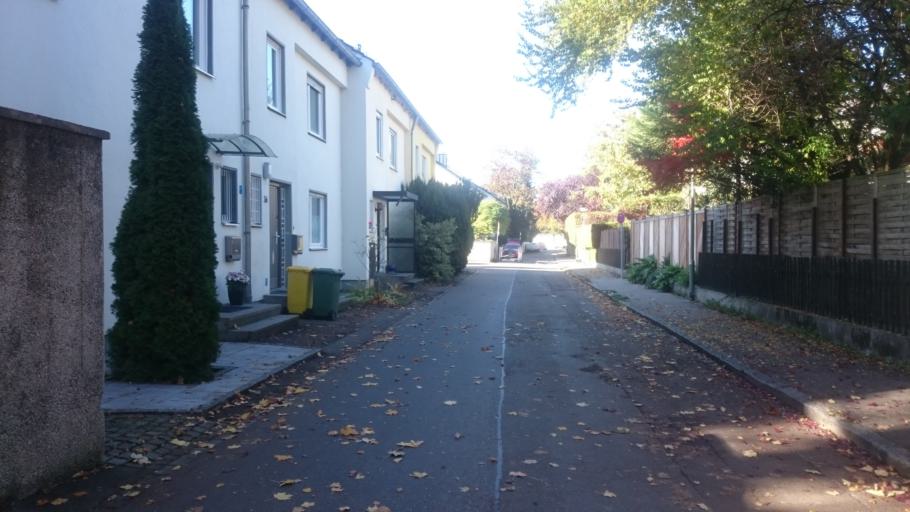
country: DE
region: Bavaria
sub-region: Swabia
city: Augsburg
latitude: 48.3574
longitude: 10.9165
